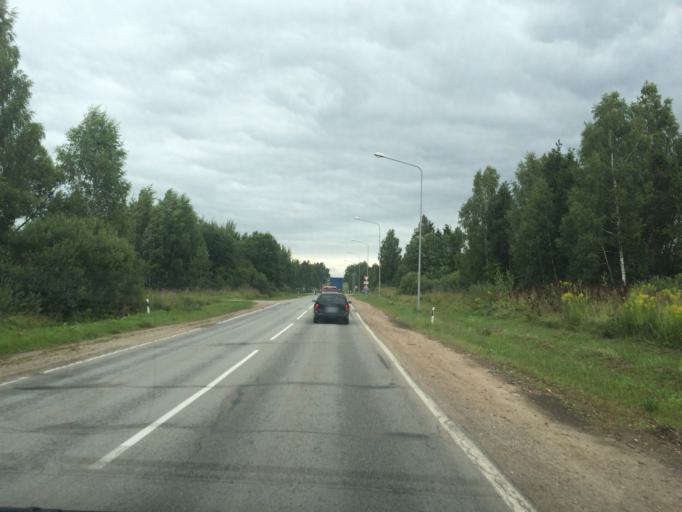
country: LV
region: Rezekne
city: Rezekne
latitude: 56.5416
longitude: 27.3524
